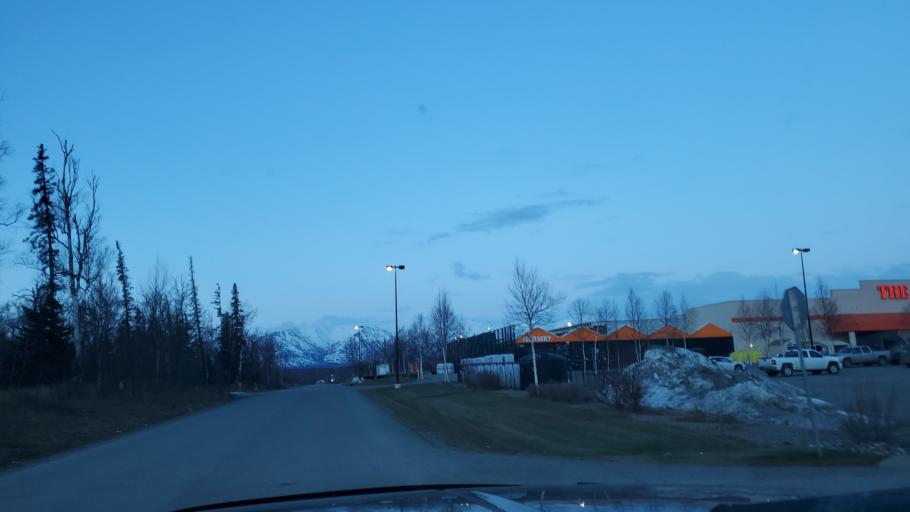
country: US
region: Alaska
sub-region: Matanuska-Susitna Borough
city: Wasilla
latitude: 61.5749
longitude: -149.4205
